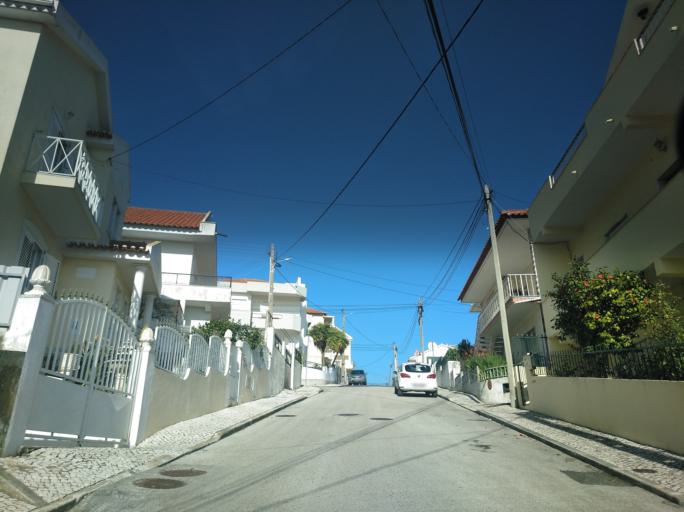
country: PT
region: Lisbon
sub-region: Odivelas
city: Famoes
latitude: 38.7914
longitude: -9.2193
